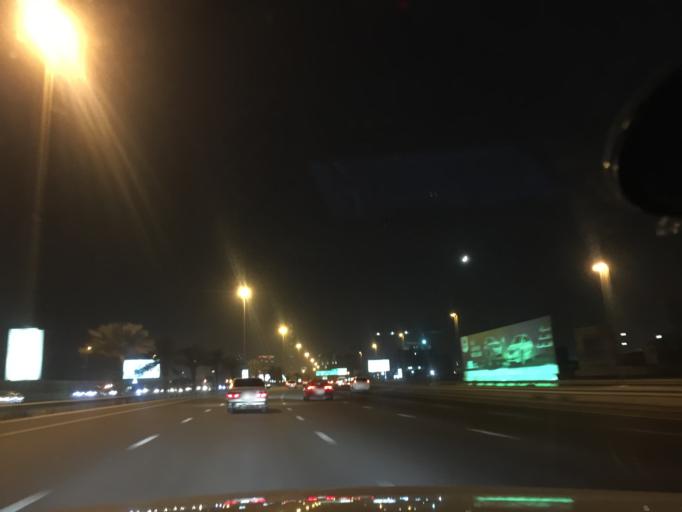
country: AE
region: Ash Shariqah
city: Sharjah
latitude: 25.2204
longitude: 55.3362
